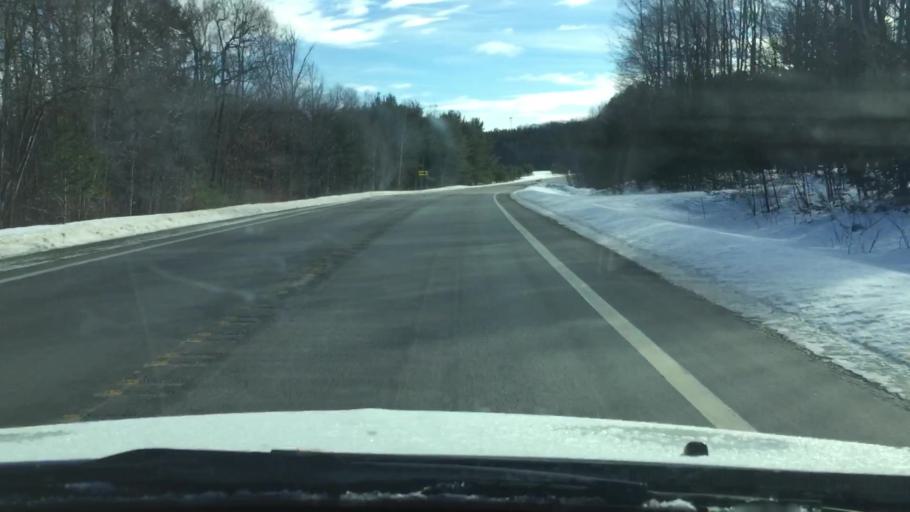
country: US
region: Michigan
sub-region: Antrim County
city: Mancelona
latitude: 44.9836
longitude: -85.0542
